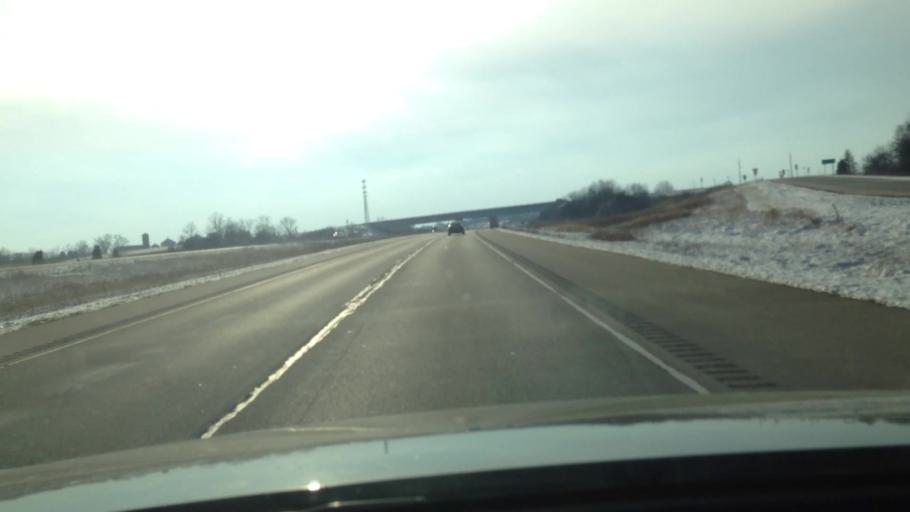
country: US
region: Wisconsin
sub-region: Walworth County
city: East Troy
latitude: 42.7509
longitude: -88.4416
